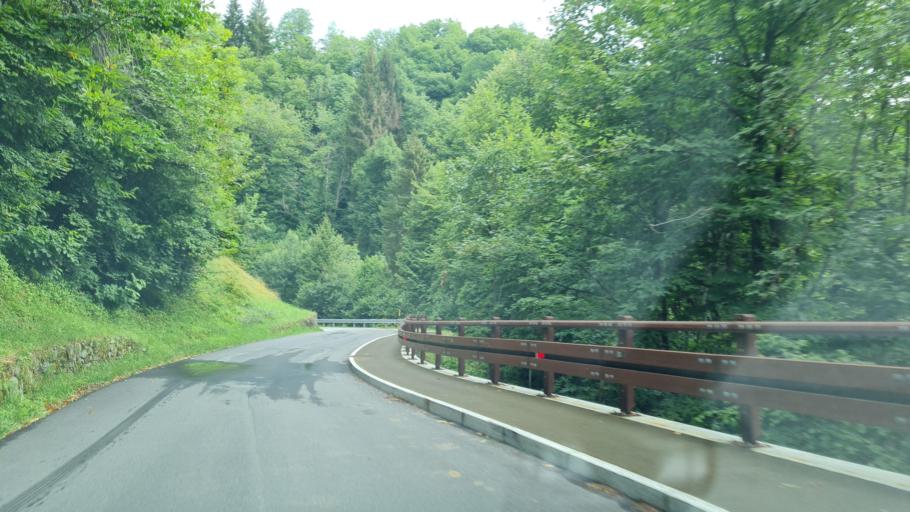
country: IT
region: Piedmont
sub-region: Provincia Verbano-Cusio-Ossola
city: Crodo
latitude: 46.2363
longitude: 8.3066
